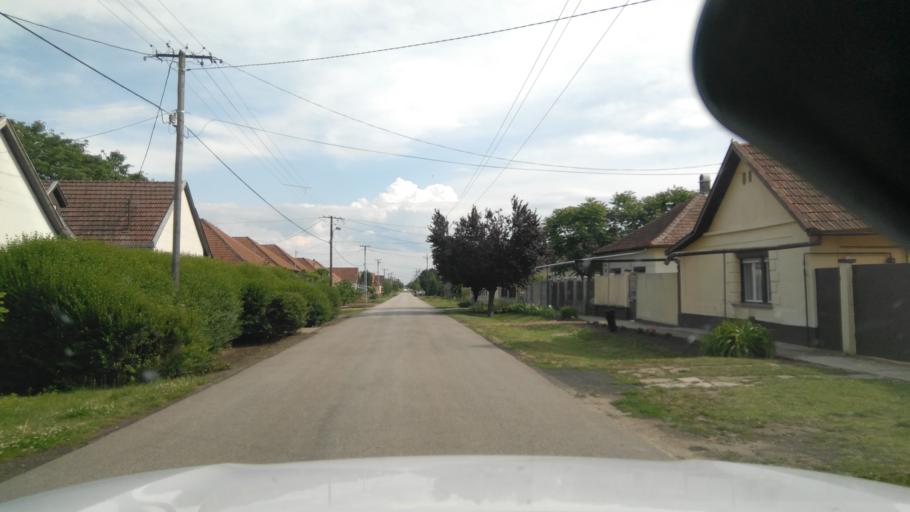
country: HU
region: Bekes
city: Ujkigyos
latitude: 46.5910
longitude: 21.0338
